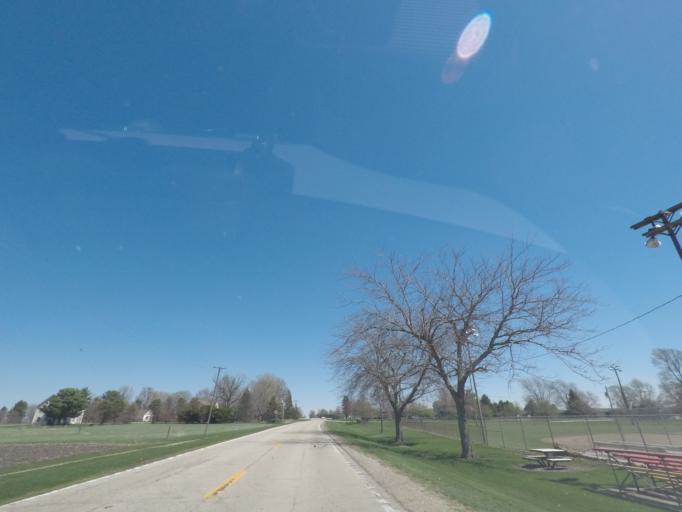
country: US
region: Illinois
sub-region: Macon County
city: Warrensburg
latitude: 39.9685
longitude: -89.1585
